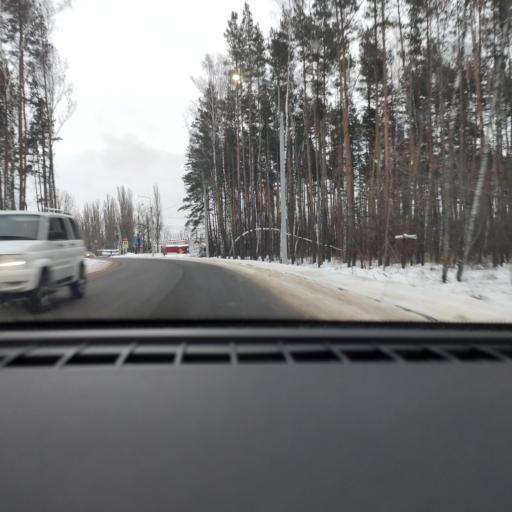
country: RU
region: Voronezj
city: Somovo
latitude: 51.7013
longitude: 39.2830
